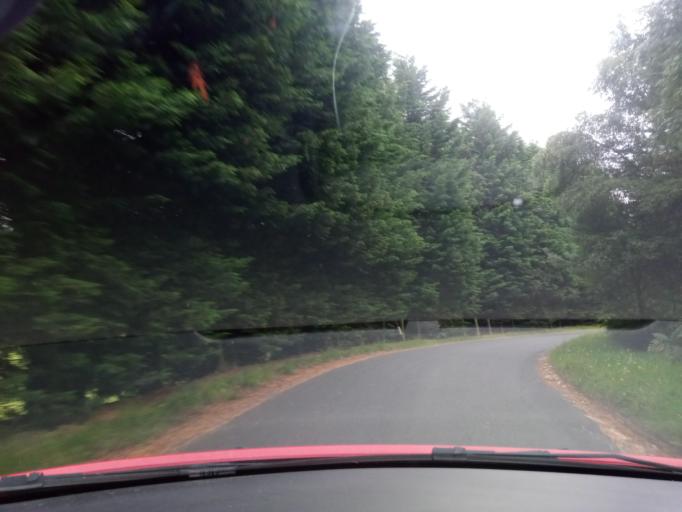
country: GB
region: England
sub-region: Northumberland
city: Rothbury
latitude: 55.2932
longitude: -2.0433
